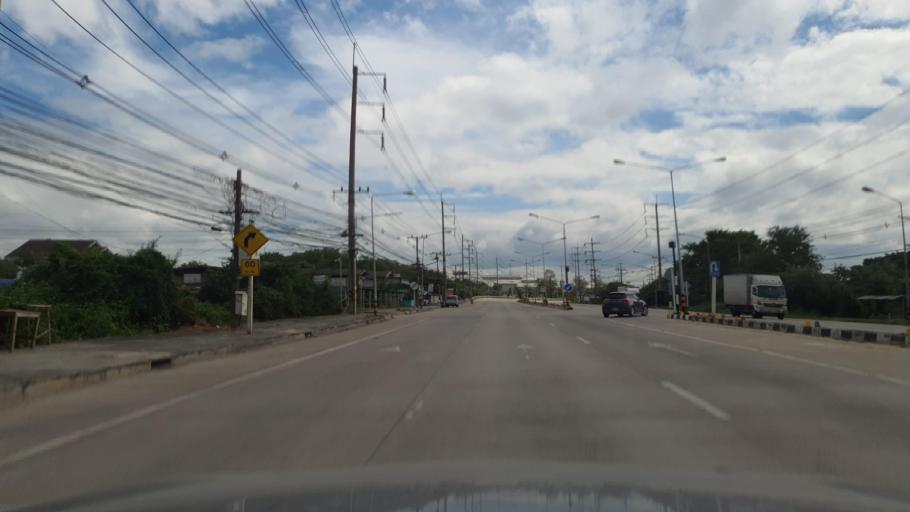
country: TH
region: Chachoengsao
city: Bang Pakong
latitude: 13.5373
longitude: 100.9903
